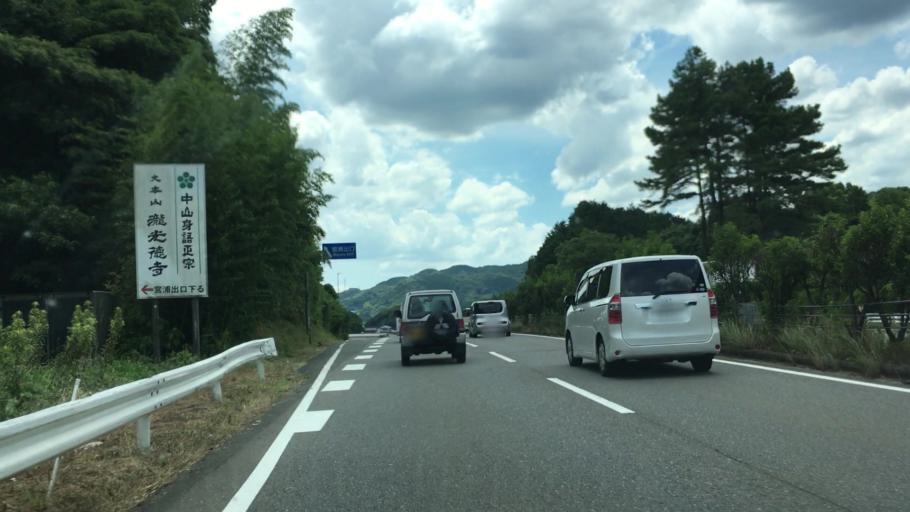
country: JP
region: Saga Prefecture
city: Tosu
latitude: 33.4291
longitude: 130.5190
